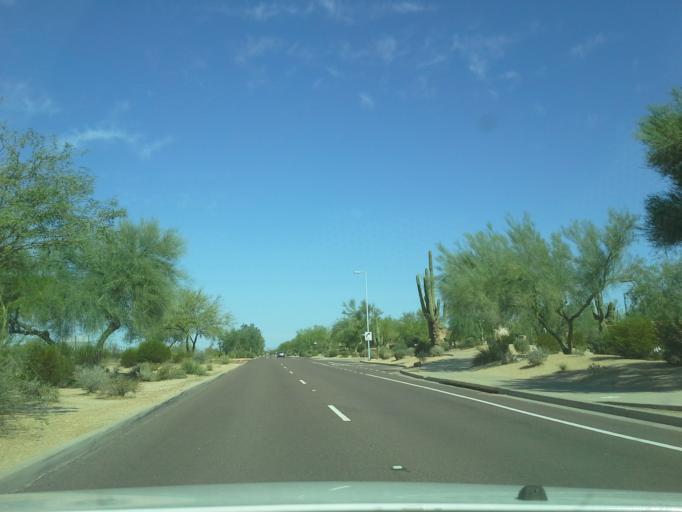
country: US
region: Arizona
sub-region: Maricopa County
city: Paradise Valley
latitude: 33.6729
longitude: -111.9084
